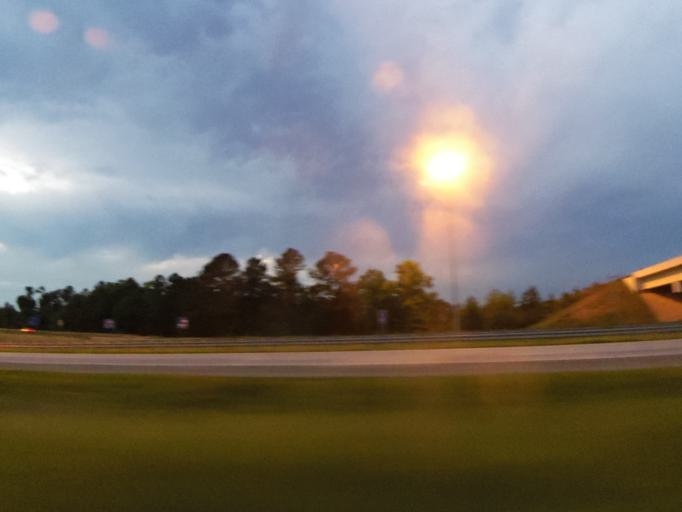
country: US
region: Georgia
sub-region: McDuffie County
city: Thomson
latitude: 33.5115
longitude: -82.4989
